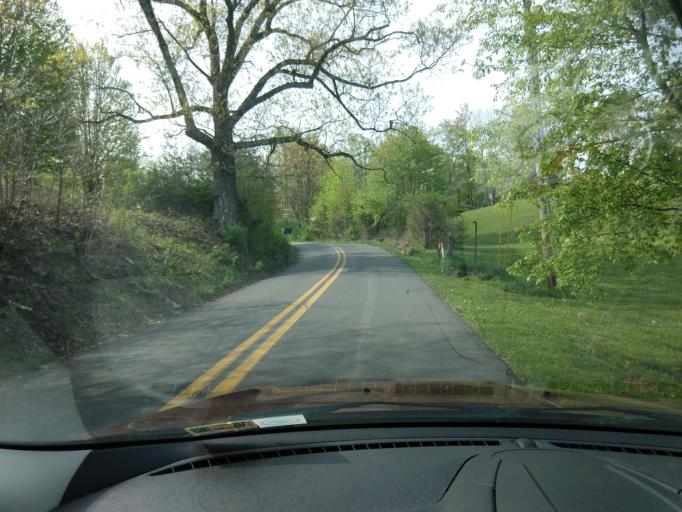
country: US
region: West Virginia
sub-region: Raleigh County
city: Crab Orchard
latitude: 37.7503
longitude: -81.2407
